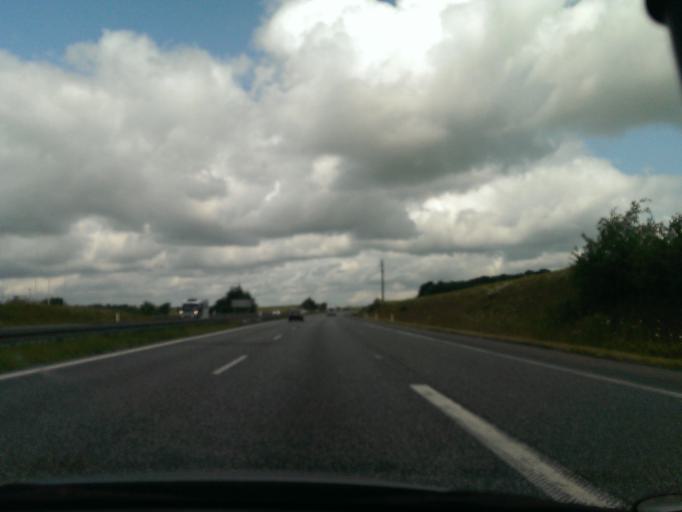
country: DK
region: North Denmark
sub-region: Mariagerfjord Kommune
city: Mariager
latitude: 56.5441
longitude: 9.8936
